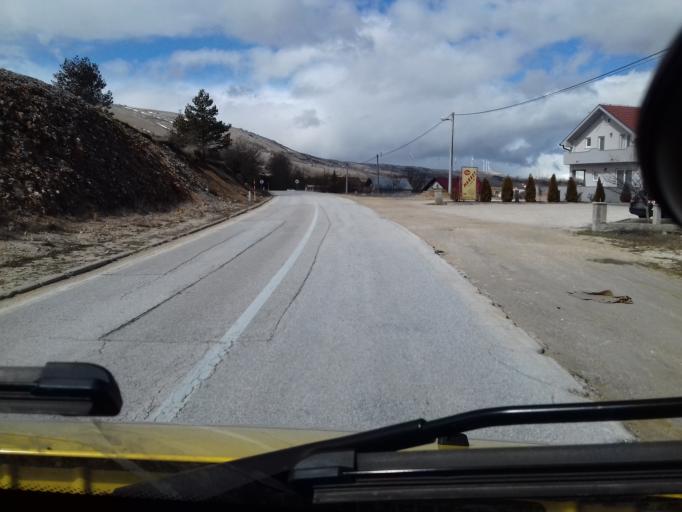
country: BA
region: Federation of Bosnia and Herzegovina
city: Dreznica
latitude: 43.5863
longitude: 17.2824
